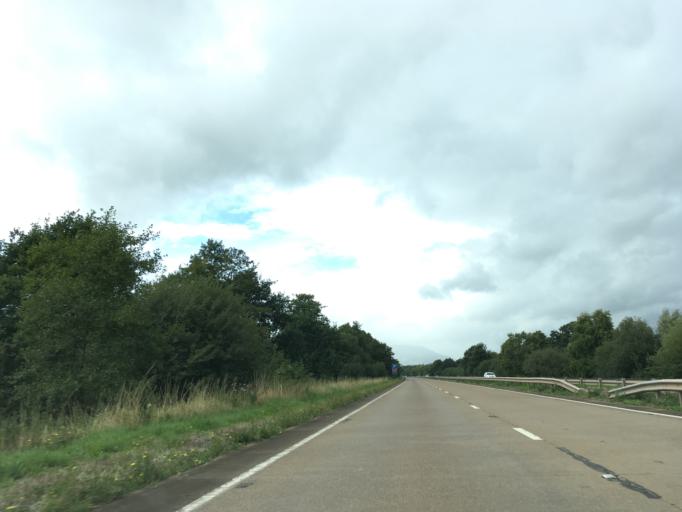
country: GB
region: Wales
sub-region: Monmouthshire
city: Llanarth
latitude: 51.7785
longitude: -2.8962
